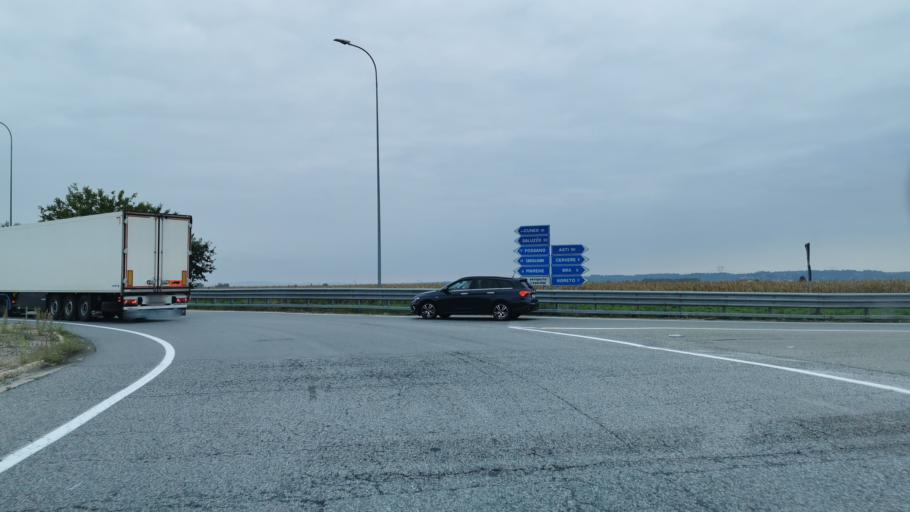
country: IT
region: Piedmont
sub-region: Provincia di Cuneo
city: Roreto
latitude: 44.6663
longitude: 7.8026
